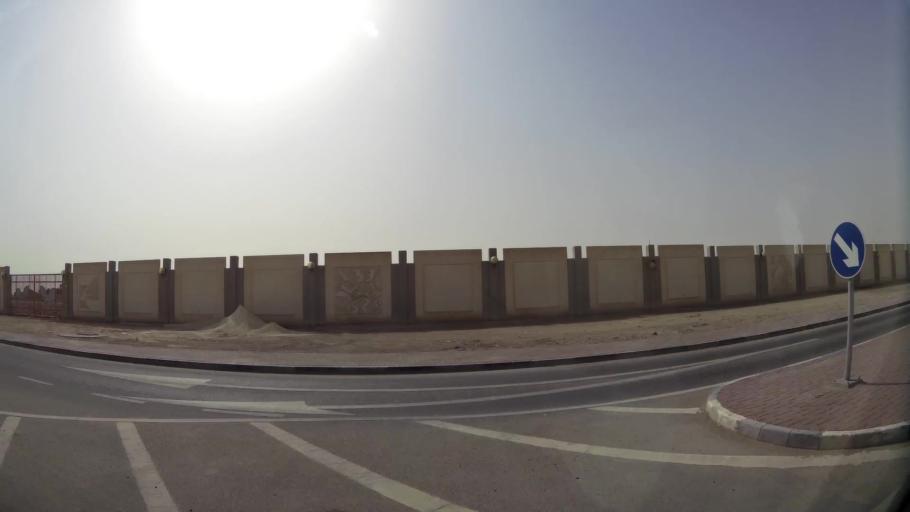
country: QA
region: Baladiyat ar Rayyan
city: Ar Rayyan
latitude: 25.2483
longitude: 51.4379
